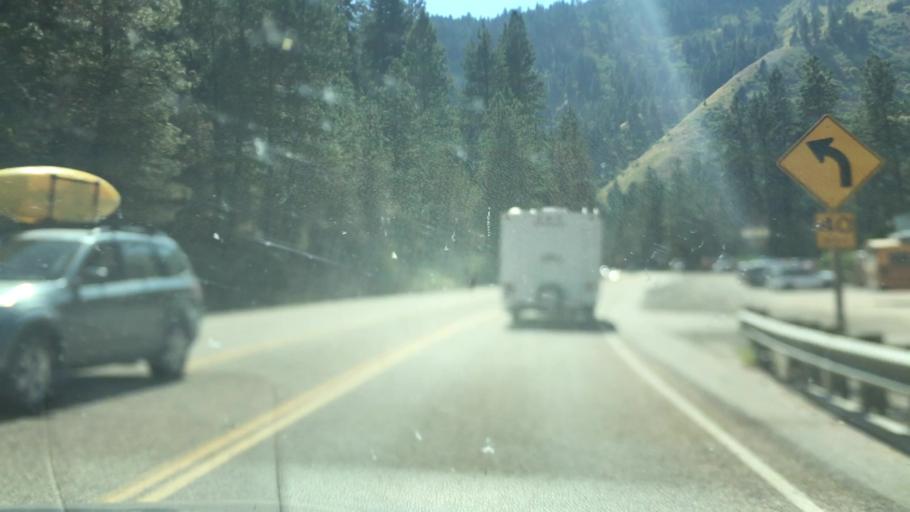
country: US
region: Idaho
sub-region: Boise County
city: Idaho City
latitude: 44.0837
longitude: -116.1162
